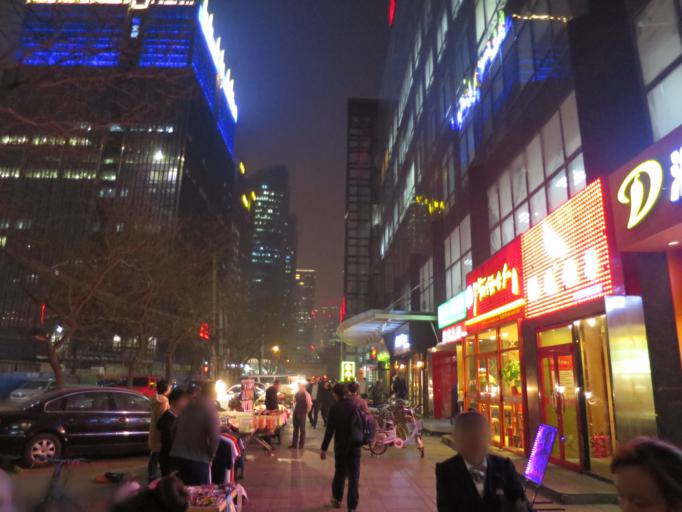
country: CN
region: Beijing
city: Chaowai
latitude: 39.9058
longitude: 116.4383
